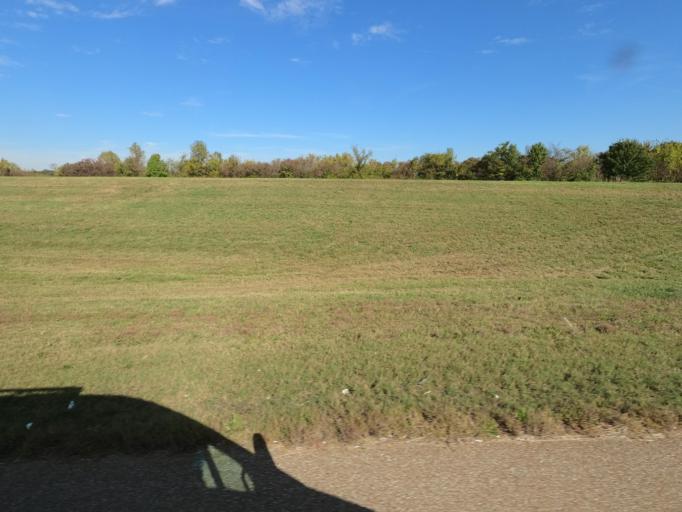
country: US
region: Tennessee
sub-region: Shelby County
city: Millington
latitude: 35.3306
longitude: -89.9190
